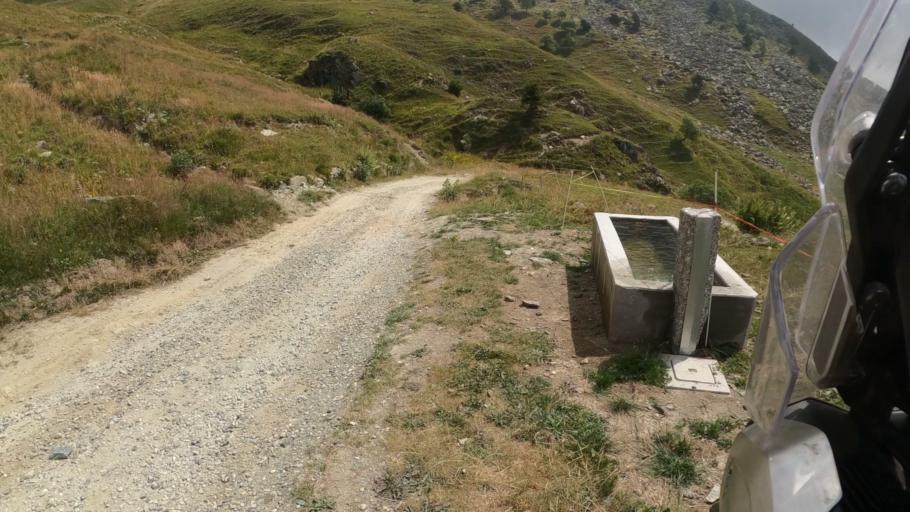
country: IT
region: Piedmont
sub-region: Provincia di Torino
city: Sant'Antonino di Susa
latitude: 45.1644
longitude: 7.2770
